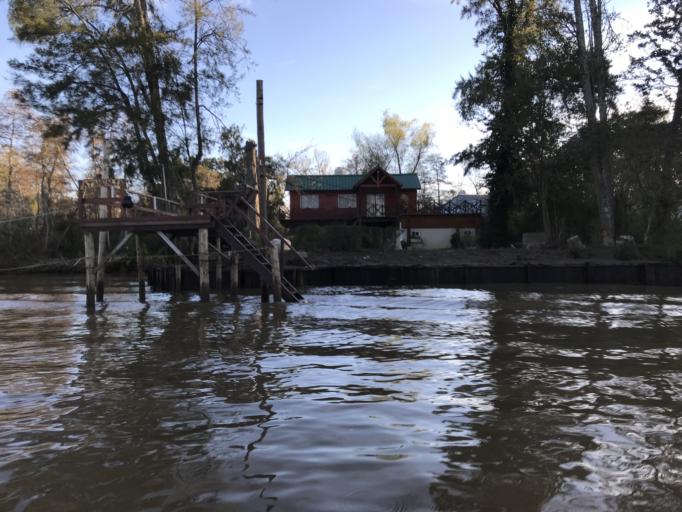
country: AR
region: Buenos Aires
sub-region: Partido de Tigre
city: Tigre
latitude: -34.3791
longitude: -58.5750
